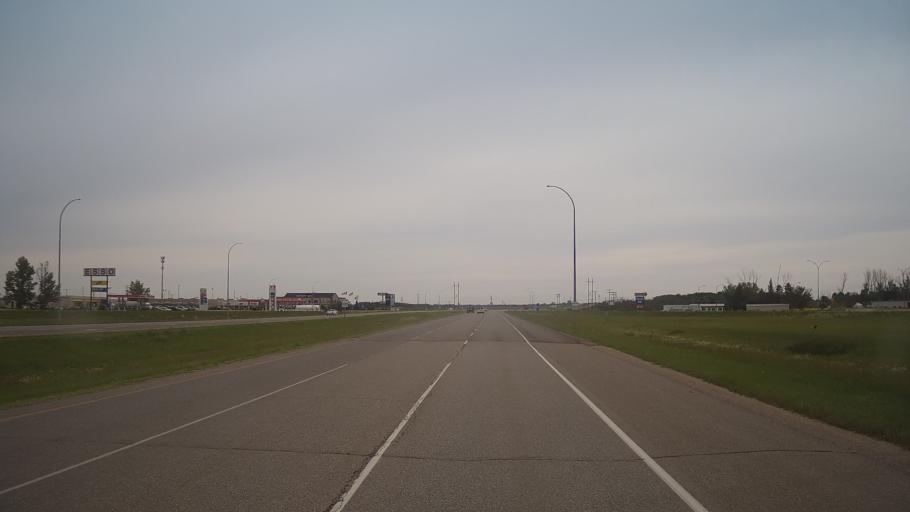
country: CA
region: Saskatchewan
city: Saskatoon
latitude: 52.0540
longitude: -106.5974
